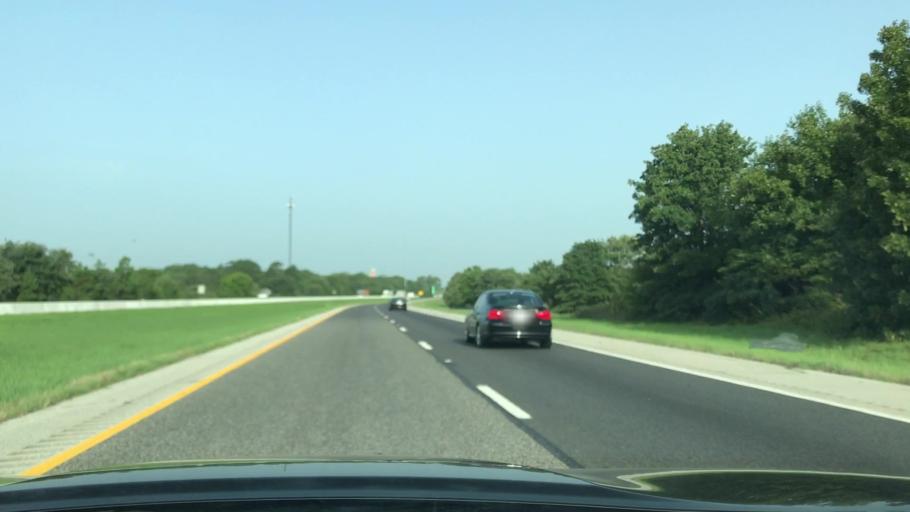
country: US
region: Texas
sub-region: Smith County
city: Tyler
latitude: 32.4521
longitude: -95.2717
